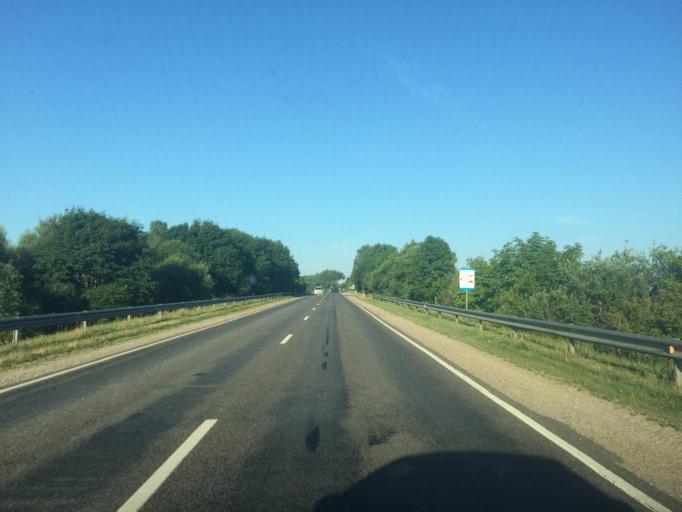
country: LT
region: Utenos apskritis
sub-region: Anyksciai
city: Anyksciai
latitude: 55.3799
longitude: 25.0337
